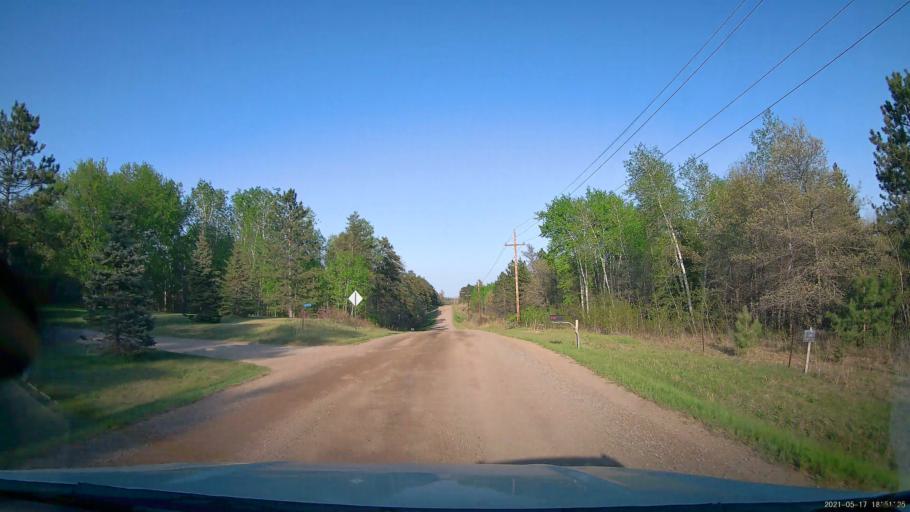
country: US
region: Minnesota
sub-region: Hubbard County
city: Park Rapids
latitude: 46.9437
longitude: -95.0131
